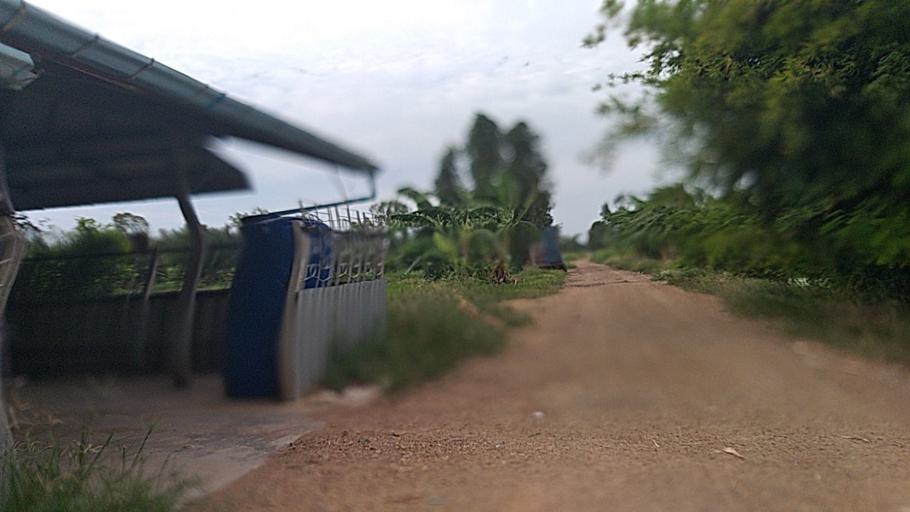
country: TH
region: Pathum Thani
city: Ban Lam Luk Ka
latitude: 14.0345
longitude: 100.8568
